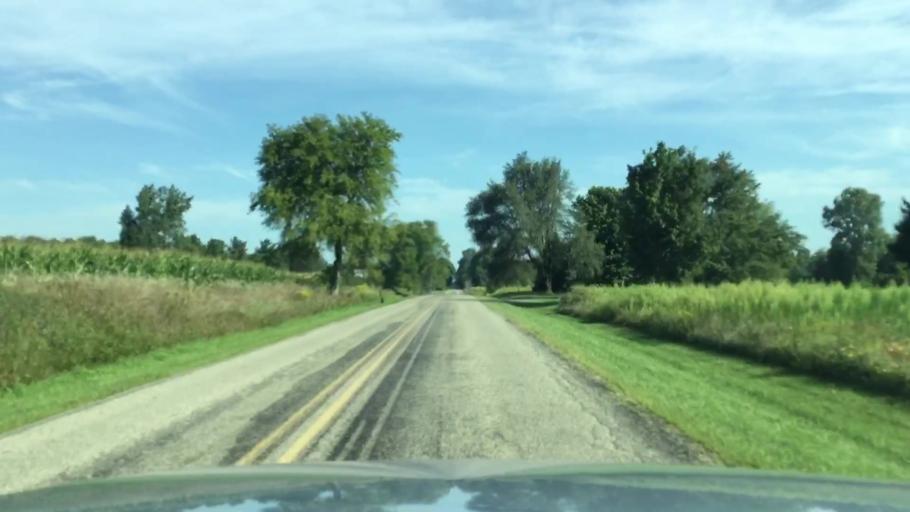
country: US
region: Michigan
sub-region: Lenawee County
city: Hudson
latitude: 41.8867
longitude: -84.4202
